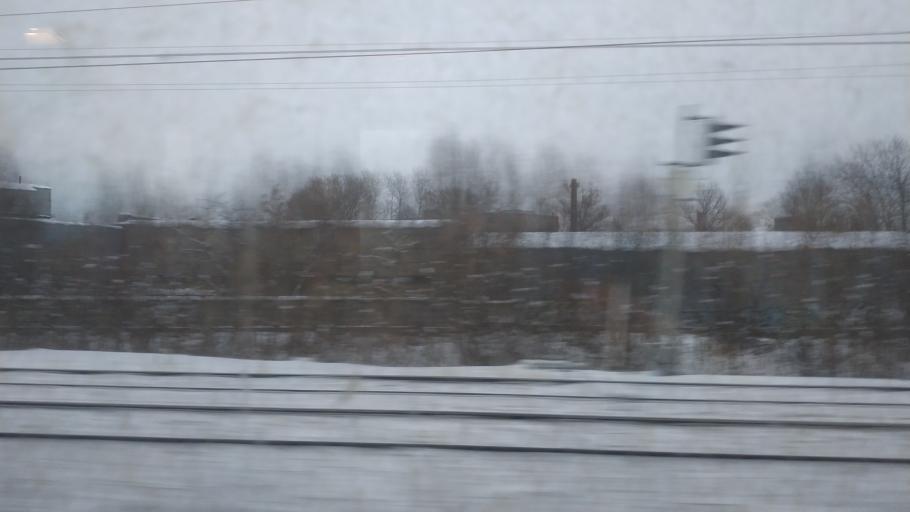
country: RU
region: Moskovskaya
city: Shcherbinka
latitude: 55.4962
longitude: 37.5581
